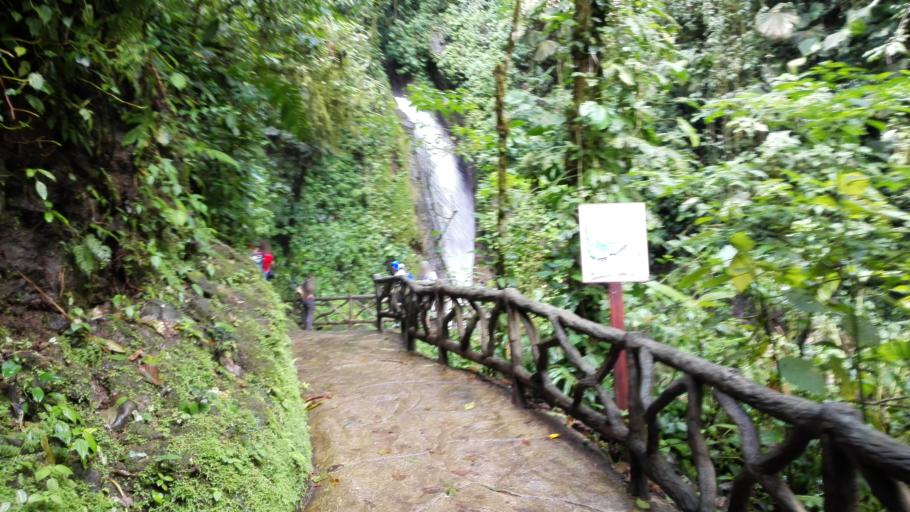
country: CR
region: Alajuela
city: La Fortuna
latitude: 10.4954
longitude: -84.7508
